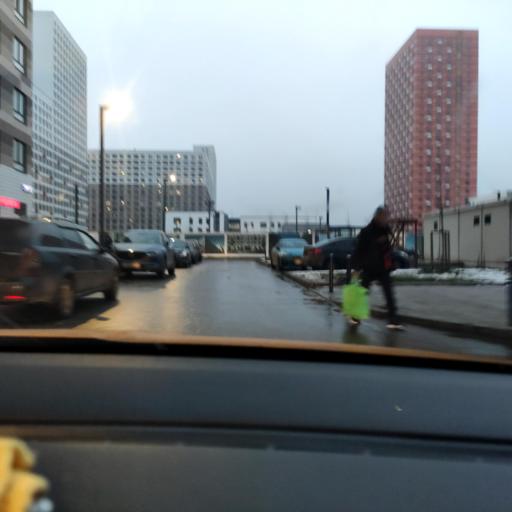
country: RU
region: Moskovskaya
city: Odintsovo
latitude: 55.6547
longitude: 37.2669
